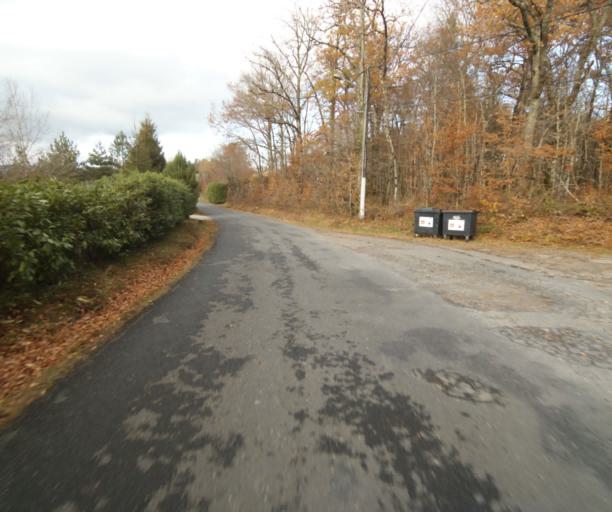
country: FR
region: Limousin
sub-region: Departement de la Correze
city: Laguenne
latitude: 45.2303
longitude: 1.7921
